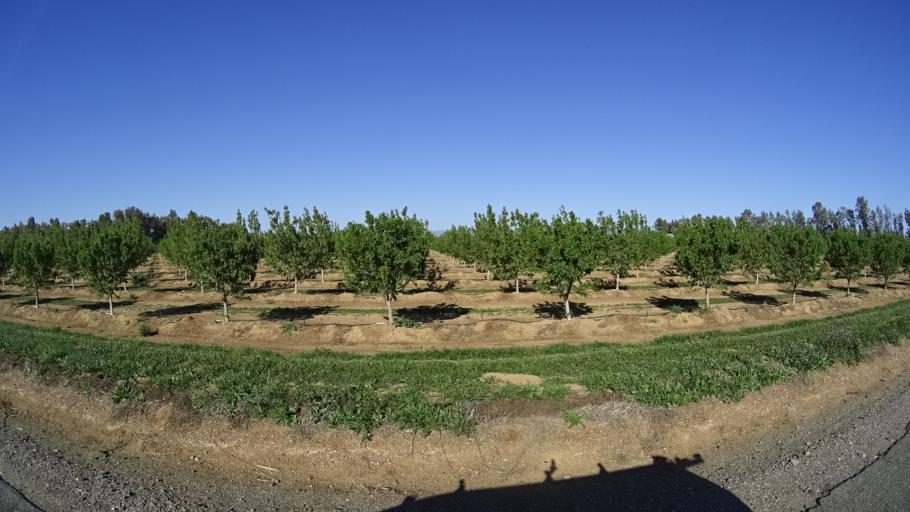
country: US
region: California
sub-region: Glenn County
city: Orland
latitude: 39.7350
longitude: -122.2390
